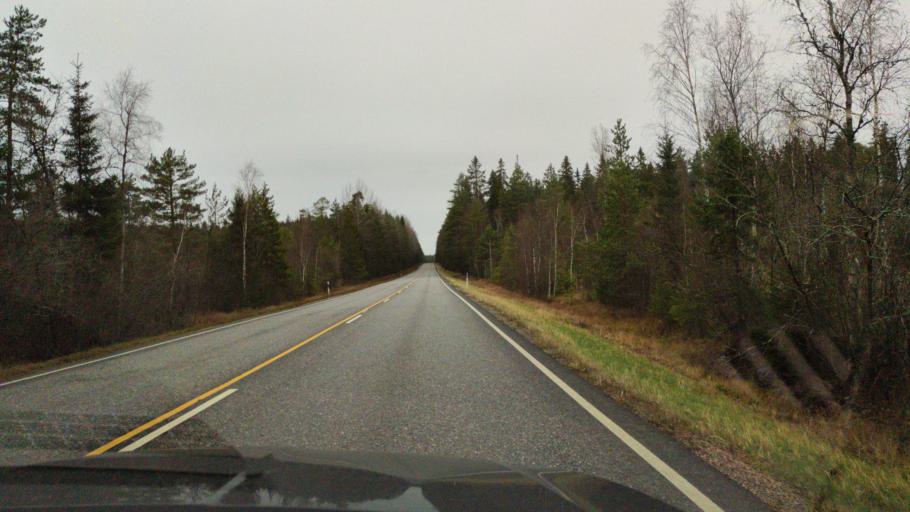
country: FI
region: Varsinais-Suomi
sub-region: Loimaa
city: Ylaene
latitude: 60.7247
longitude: 22.4435
